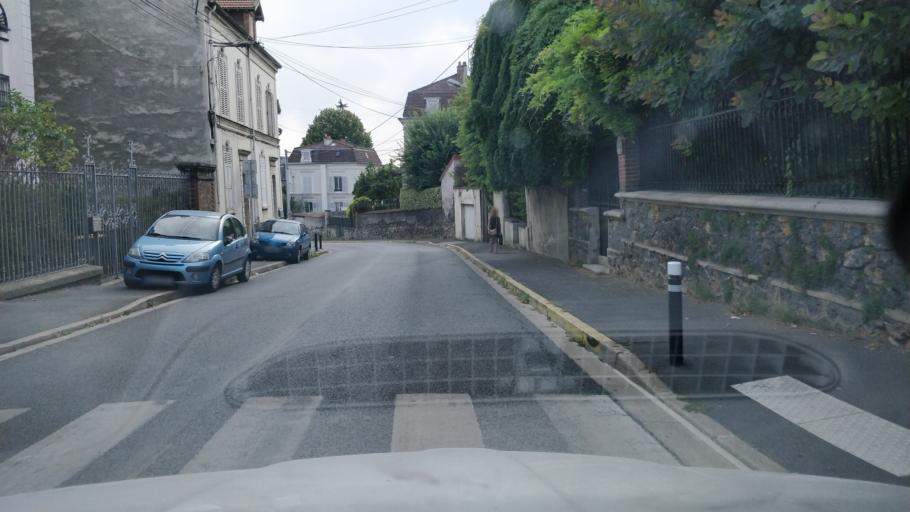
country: FR
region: Ile-de-France
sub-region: Departement de Seine-et-Marne
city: Thorigny-sur-Marne
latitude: 48.8833
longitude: 2.7054
